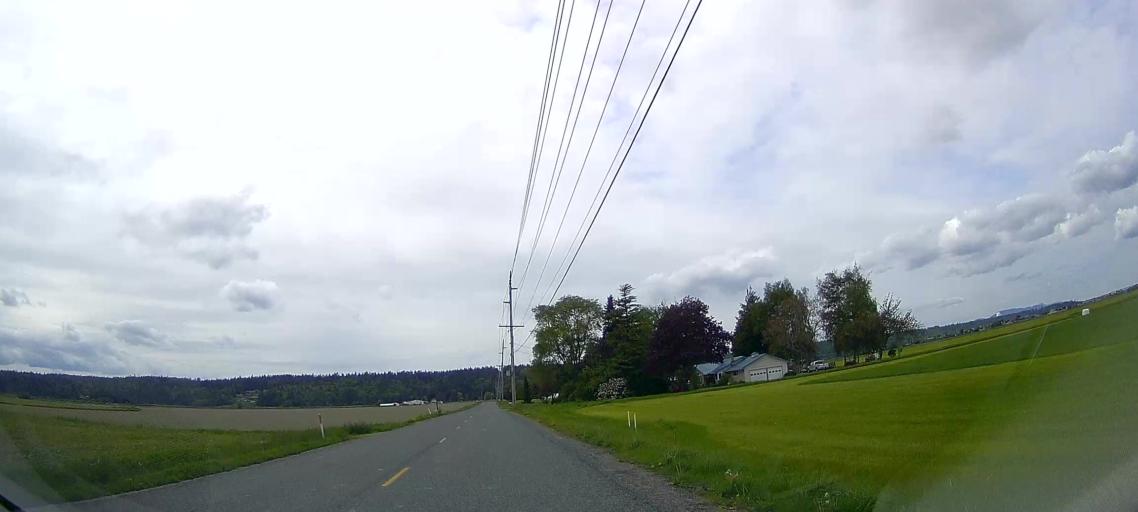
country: US
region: Washington
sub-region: Skagit County
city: Mount Vernon
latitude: 48.4210
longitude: -122.4811
